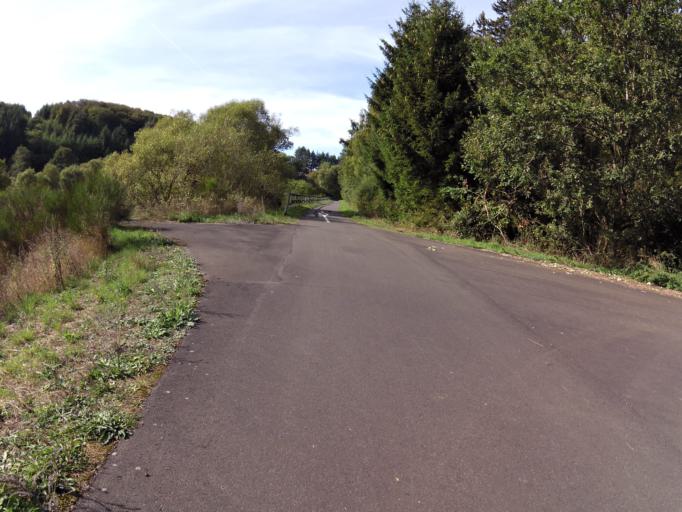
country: DE
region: Rheinland-Pfalz
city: Habscheid
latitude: 50.1932
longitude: 6.2890
